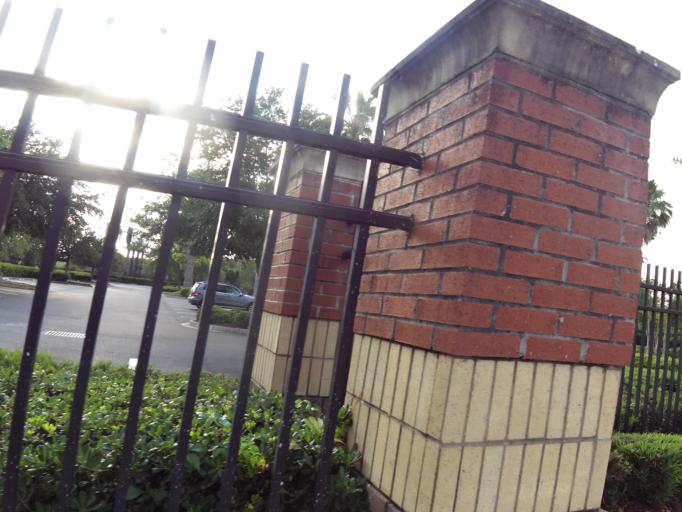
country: US
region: Florida
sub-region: Duval County
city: Jacksonville
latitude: 30.3335
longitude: -81.6688
